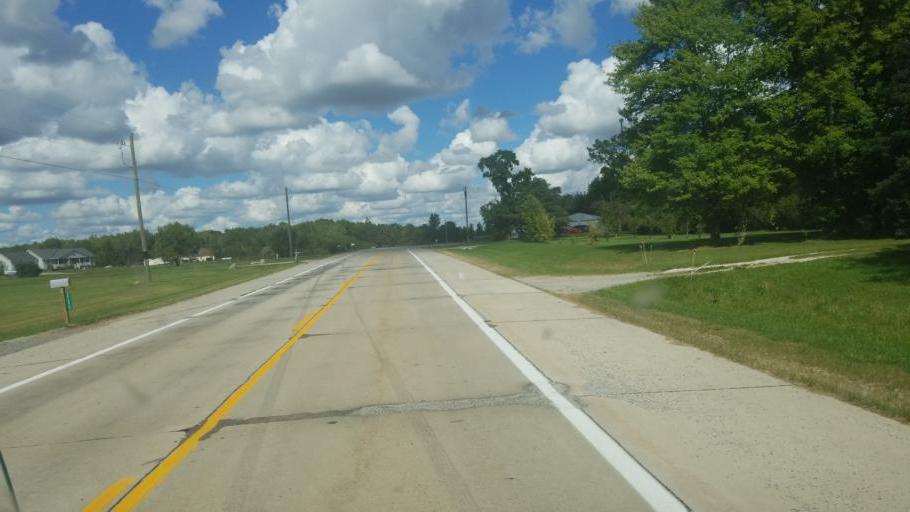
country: US
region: Ohio
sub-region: Champaign County
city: North Lewisburg
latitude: 40.3062
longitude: -83.5100
